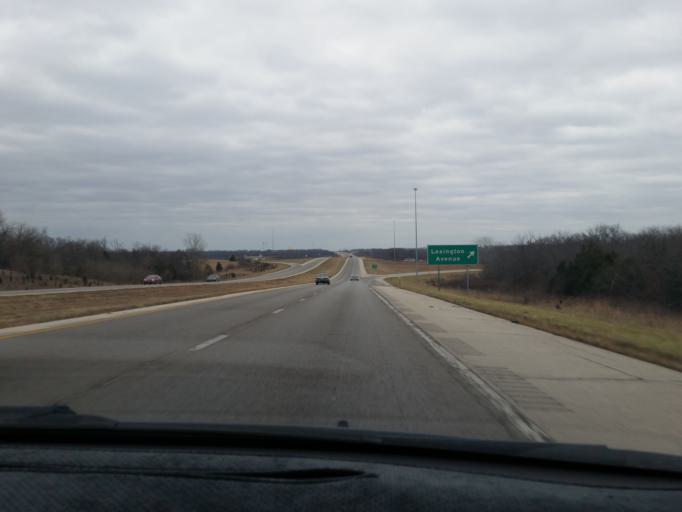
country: US
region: Kansas
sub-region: Johnson County
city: De Soto
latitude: 38.9610
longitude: -94.9930
